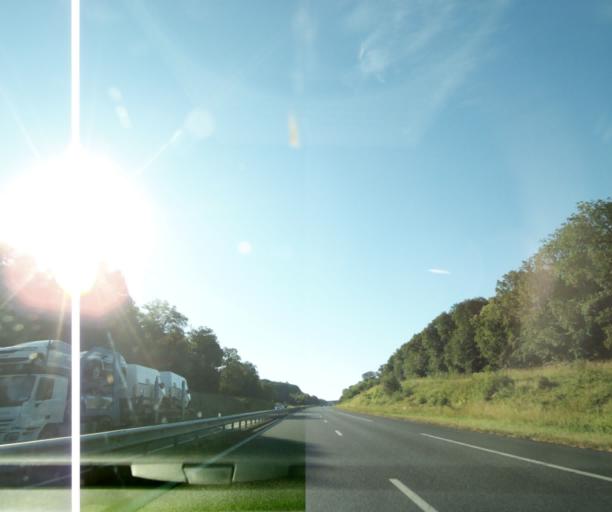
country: FR
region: Bourgogne
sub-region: Departement de l'Yonne
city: Soucy
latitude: 48.2418
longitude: 3.3629
